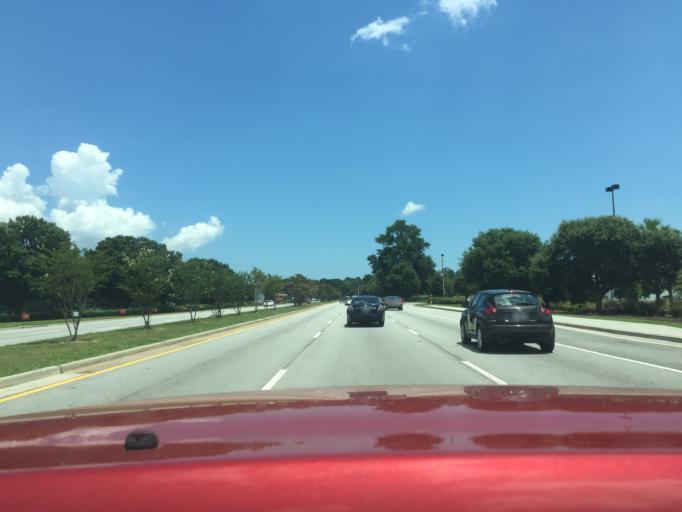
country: US
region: Georgia
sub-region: Chatham County
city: Georgetown
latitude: 31.9818
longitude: -81.1732
